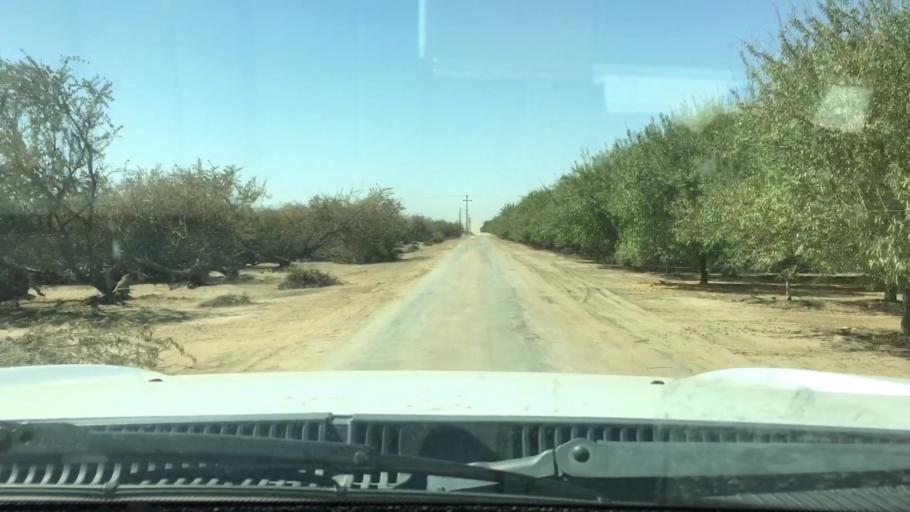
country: US
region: California
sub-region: Kern County
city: Shafter
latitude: 35.4563
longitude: -119.3113
